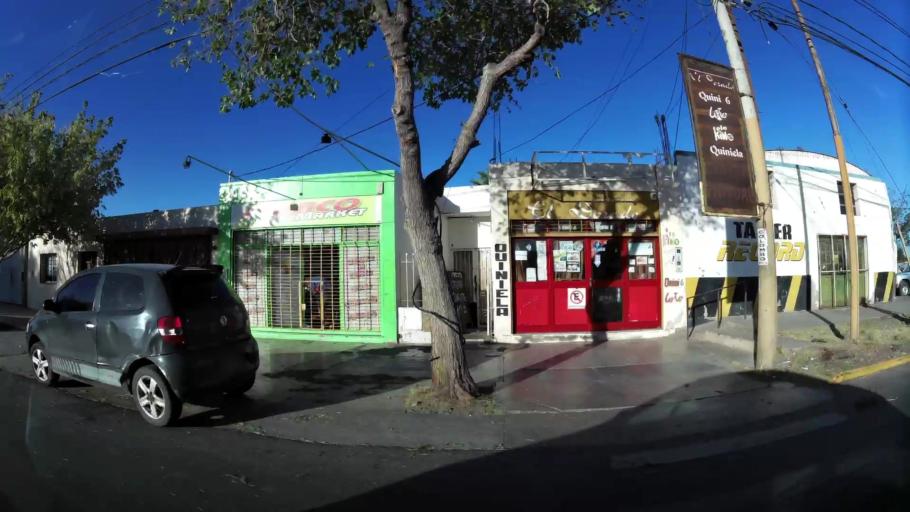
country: AR
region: San Juan
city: San Juan
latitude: -31.5512
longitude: -68.5266
